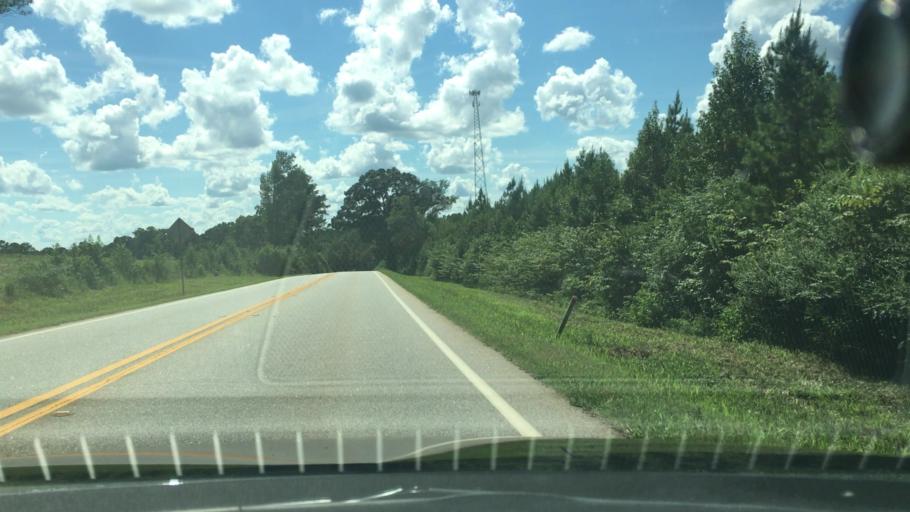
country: US
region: Georgia
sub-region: Butts County
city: Indian Springs
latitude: 33.3093
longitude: -83.8161
